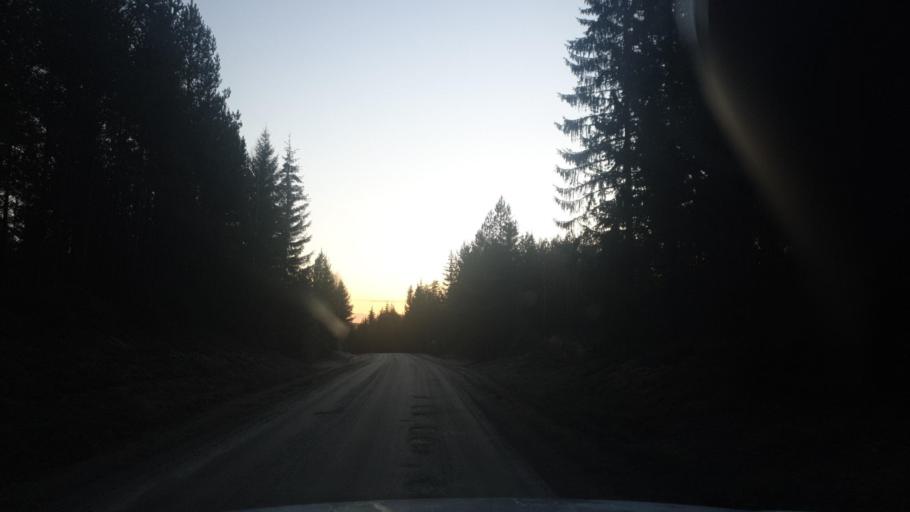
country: SE
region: Vaermland
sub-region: Eda Kommun
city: Charlottenberg
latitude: 59.9841
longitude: 12.4148
